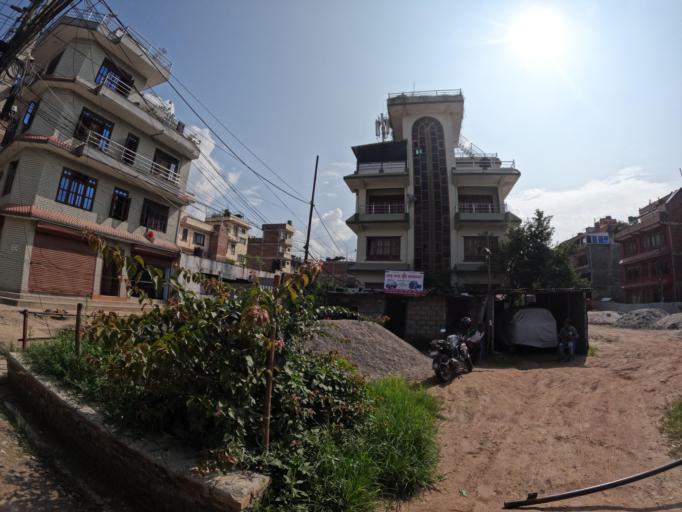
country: NP
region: Central Region
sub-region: Bagmati Zone
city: Bhaktapur
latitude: 27.6776
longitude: 85.4424
